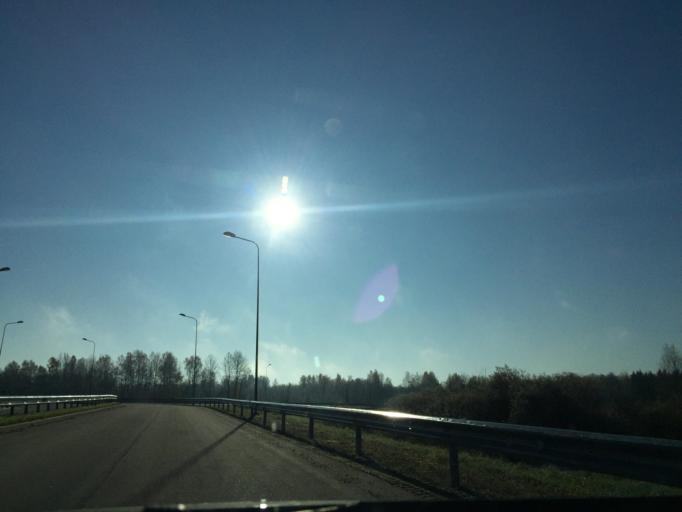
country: LV
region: Aizkraukles Rajons
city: Aizkraukle
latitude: 56.7009
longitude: 25.2805
